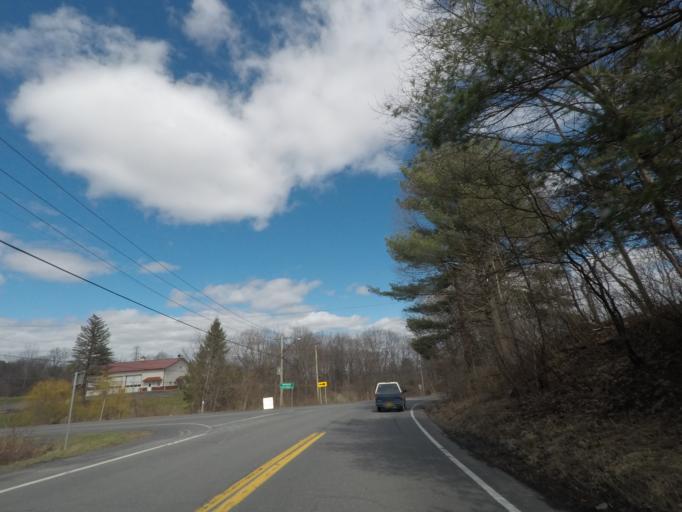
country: US
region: New York
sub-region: Albany County
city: Delmar
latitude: 42.5766
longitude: -73.8850
